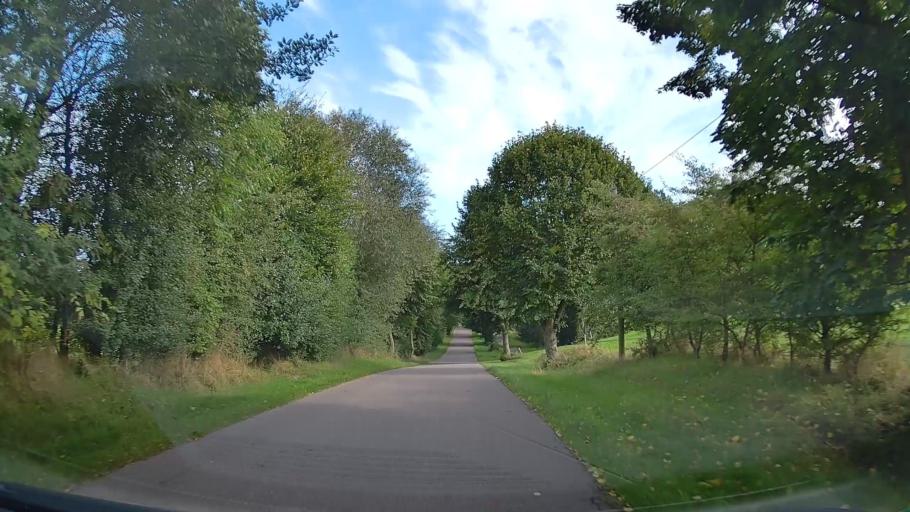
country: DE
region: Schleswig-Holstein
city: Ringsberg
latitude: 54.8314
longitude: 9.5912
